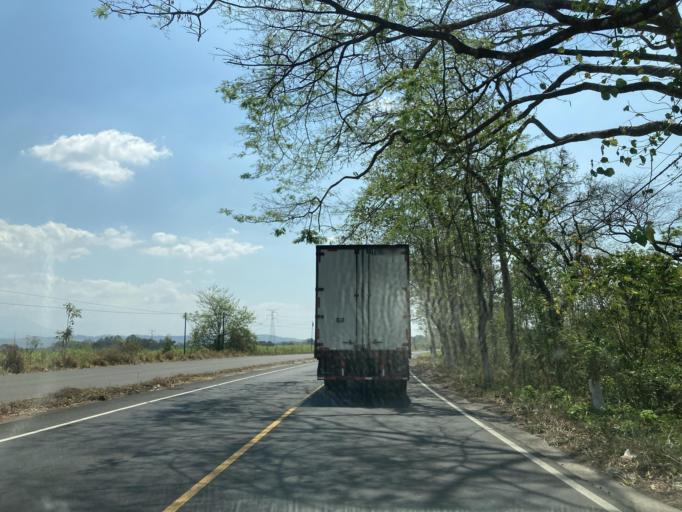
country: GT
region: Escuintla
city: Guanagazapa
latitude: 14.1985
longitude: -90.6999
